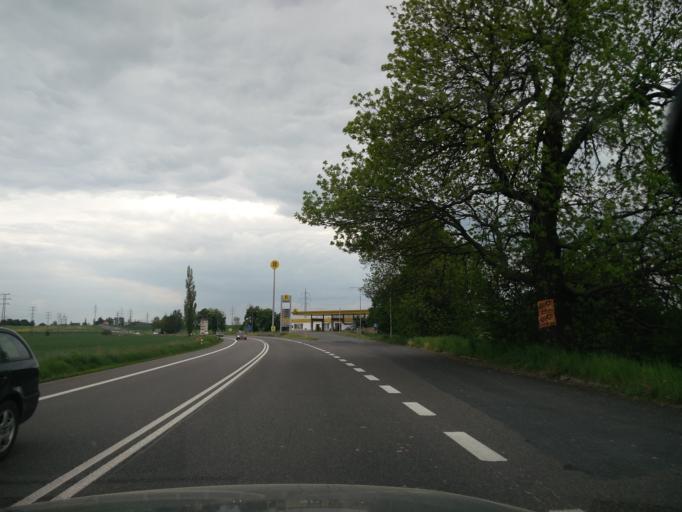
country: CZ
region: Jihocesky
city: Mirovice
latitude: 49.5248
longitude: 14.0732
